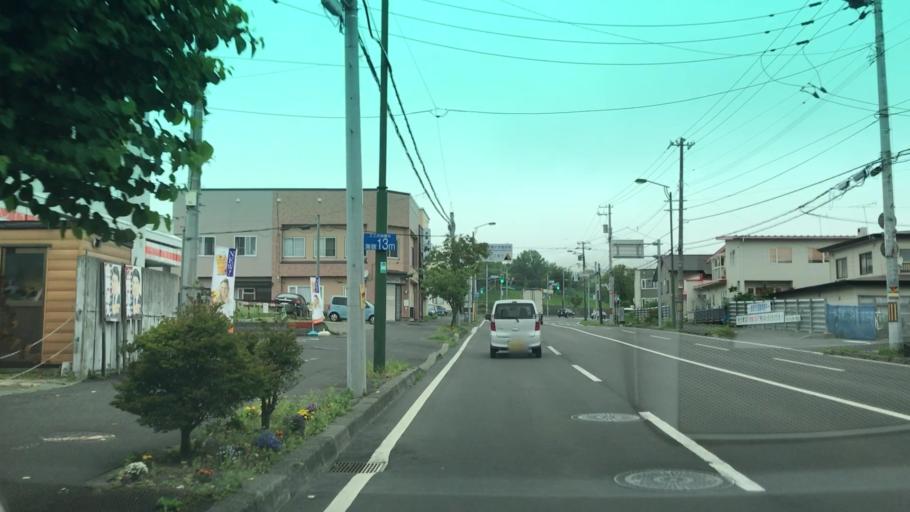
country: JP
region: Hokkaido
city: Muroran
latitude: 42.3644
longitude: 141.0375
